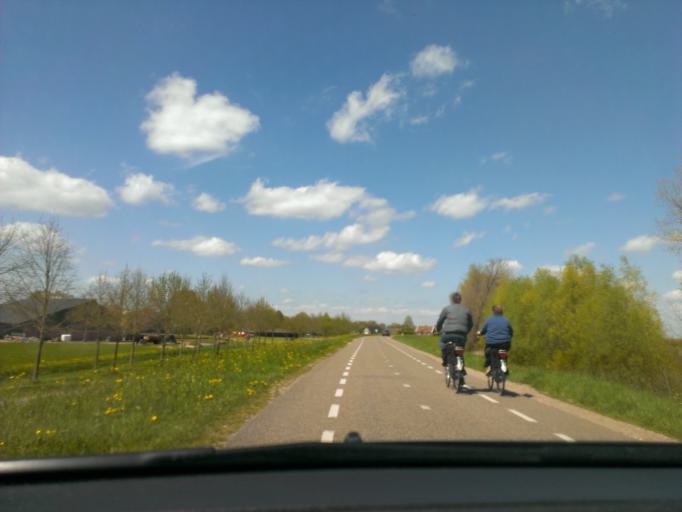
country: NL
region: Overijssel
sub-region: Gemeente Olst-Wijhe
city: Olst
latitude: 52.3233
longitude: 6.0889
